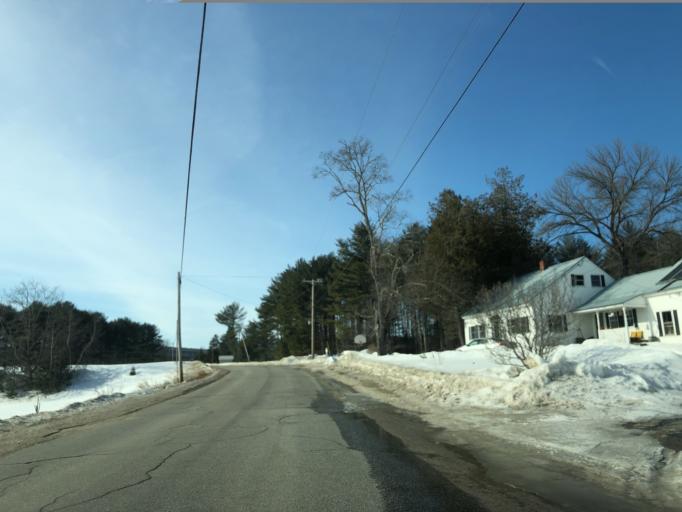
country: US
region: Maine
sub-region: Oxford County
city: Buckfield
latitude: 44.2985
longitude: -70.3795
